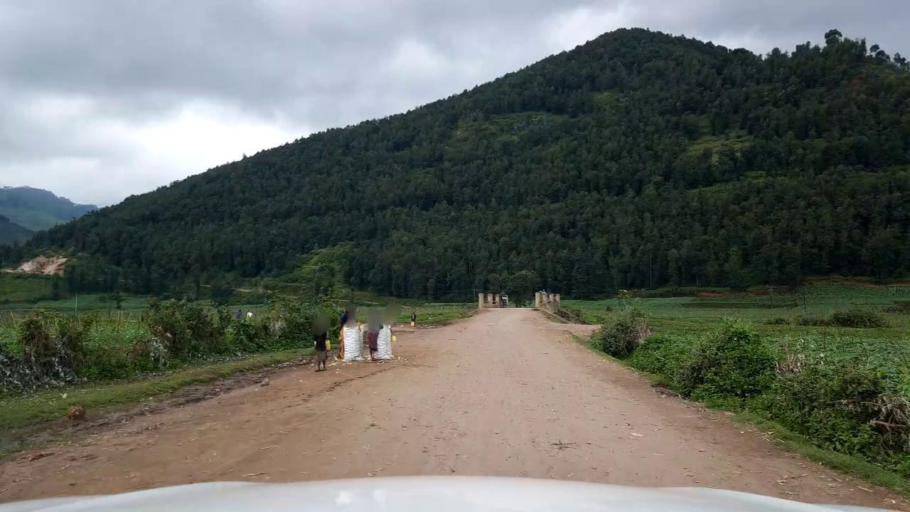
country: RW
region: Western Province
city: Gisenyi
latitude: -1.6451
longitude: 29.4103
